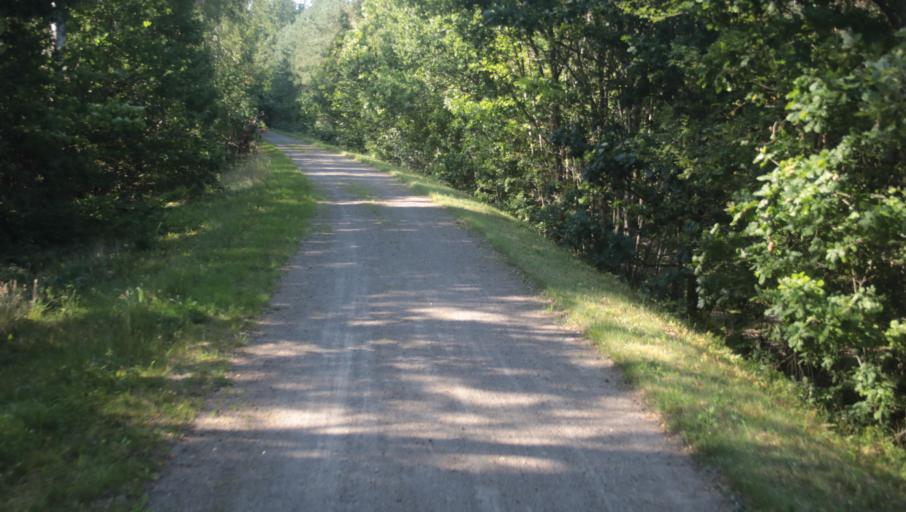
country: SE
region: Blekinge
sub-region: Karlshamns Kommun
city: Svangsta
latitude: 56.2857
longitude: 14.7520
